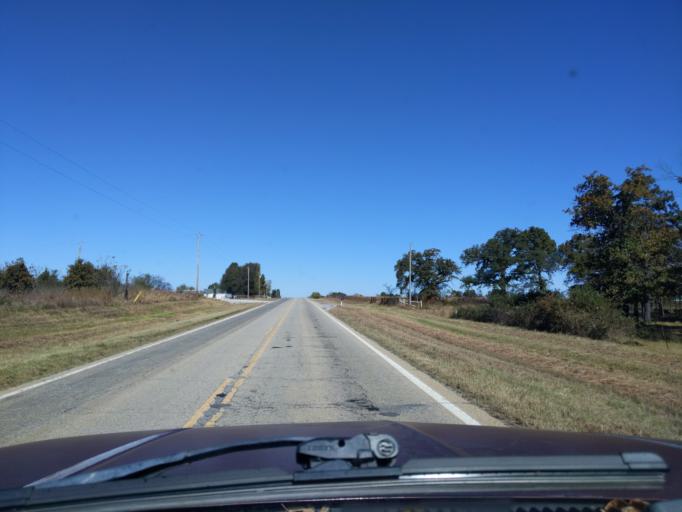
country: US
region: Oklahoma
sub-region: Creek County
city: Bristow
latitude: 35.7184
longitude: -96.3872
